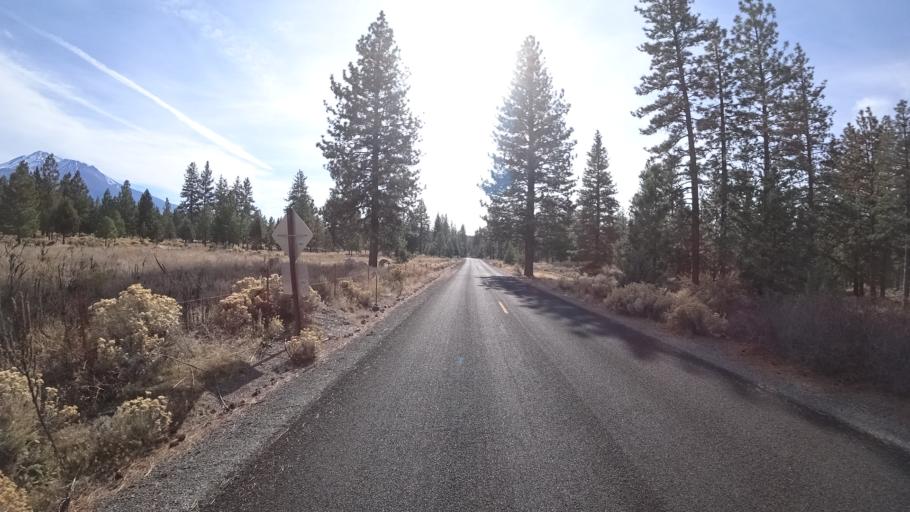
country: US
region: California
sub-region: Siskiyou County
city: Weed
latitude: 41.4967
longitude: -122.3807
